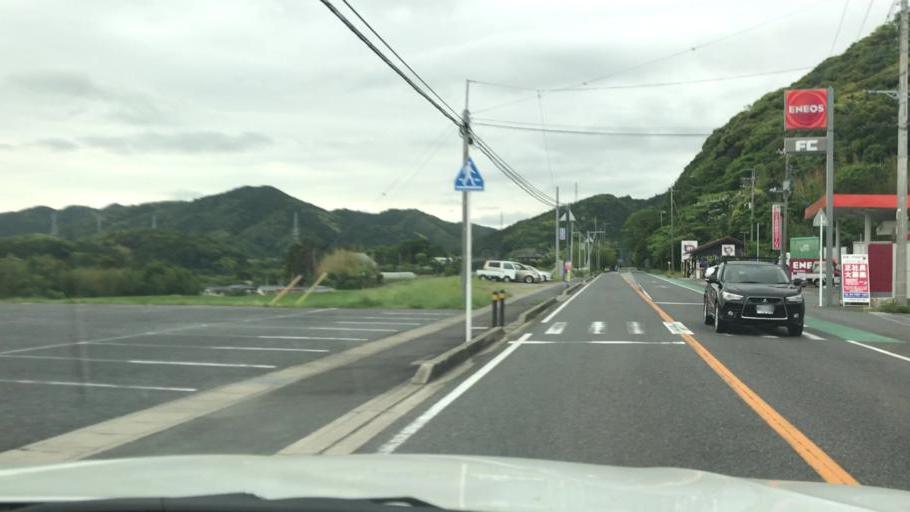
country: JP
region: Chiba
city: Kawaguchi
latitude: 35.1261
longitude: 140.0800
